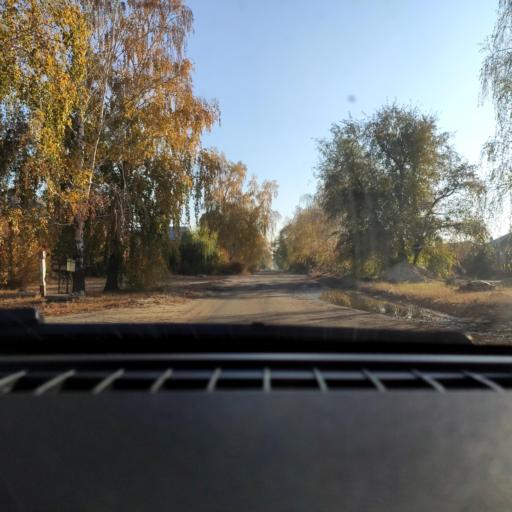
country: RU
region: Voronezj
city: Maslovka
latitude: 51.6295
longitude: 39.2700
